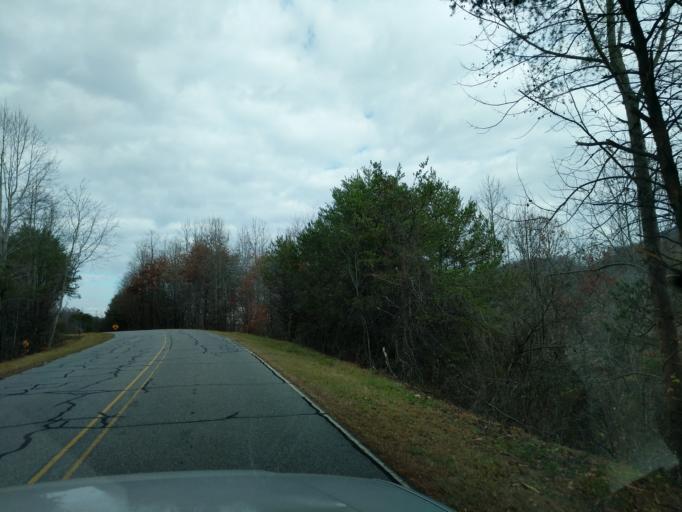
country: US
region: North Carolina
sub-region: McDowell County
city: West Marion
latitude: 35.6426
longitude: -81.9885
